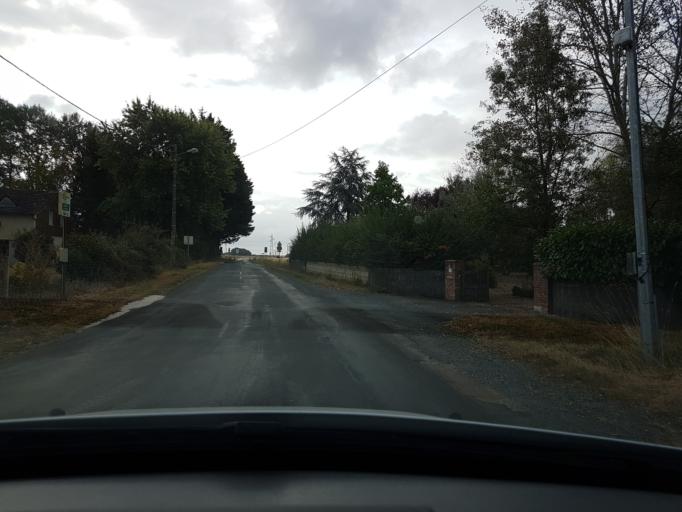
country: FR
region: Centre
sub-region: Departement d'Indre-et-Loire
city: Larcay
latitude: 47.3468
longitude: 0.7769
